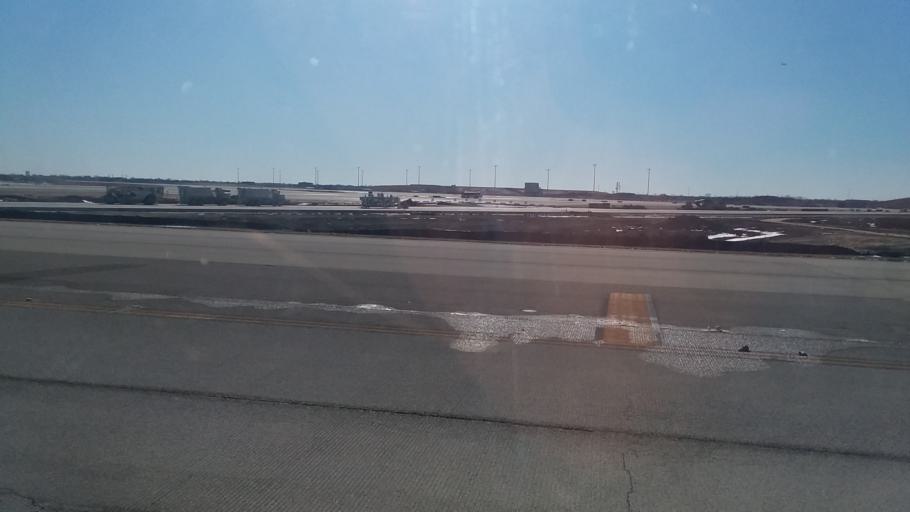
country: US
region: Illinois
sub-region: DuPage County
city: Bensenville
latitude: 41.9831
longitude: -87.9246
